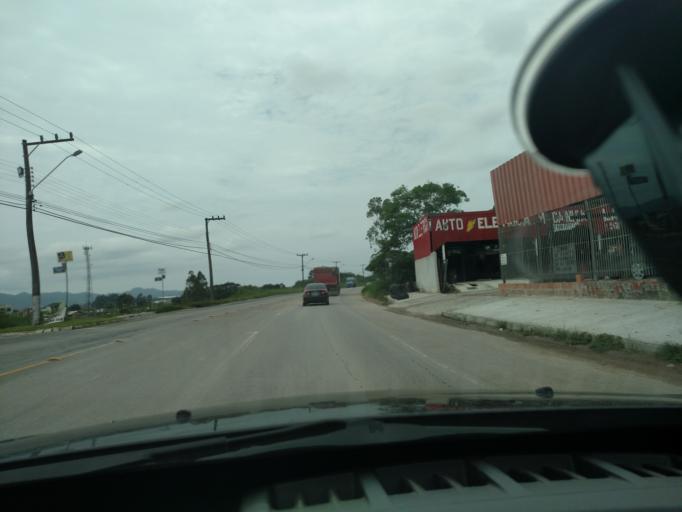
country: BR
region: Santa Catarina
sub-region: Itajai
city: Itajai
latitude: -26.8865
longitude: -48.7494
